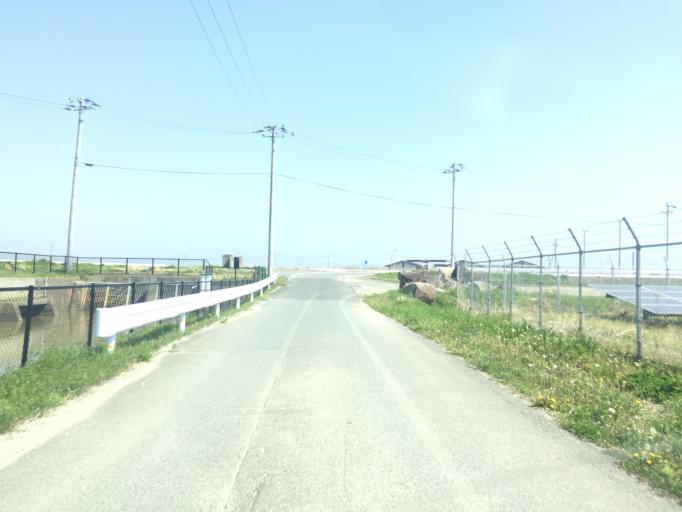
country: JP
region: Miyagi
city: Marumori
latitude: 37.7747
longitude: 140.9776
